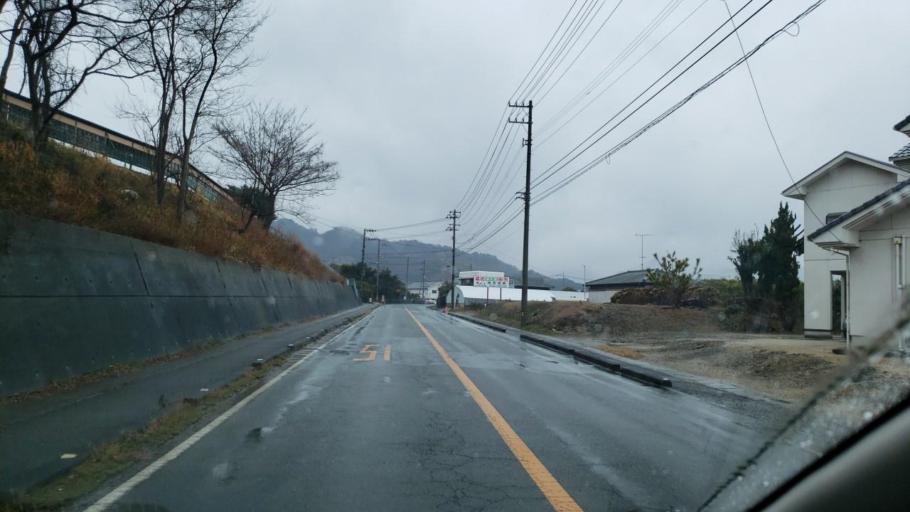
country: JP
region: Tokushima
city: Ishii
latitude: 34.1535
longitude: 134.4908
